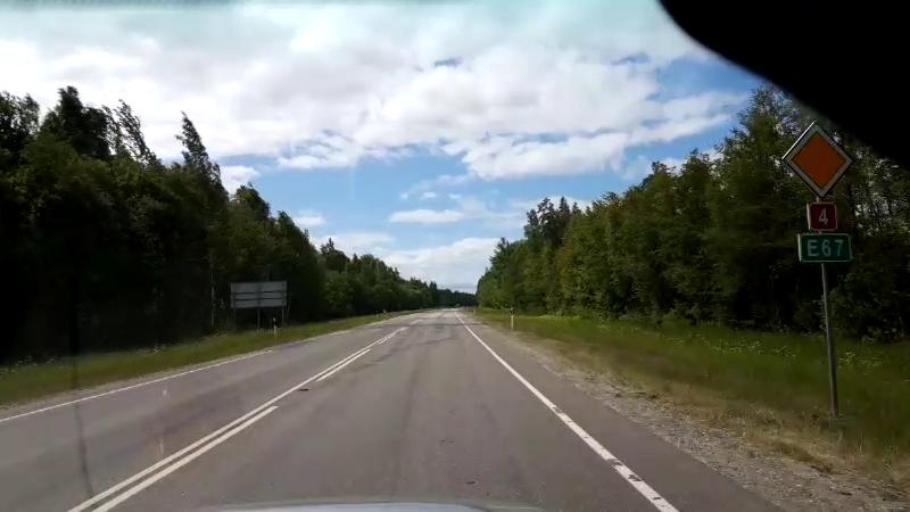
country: LV
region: Salacgrivas
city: Ainazi
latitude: 58.0271
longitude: 24.5028
